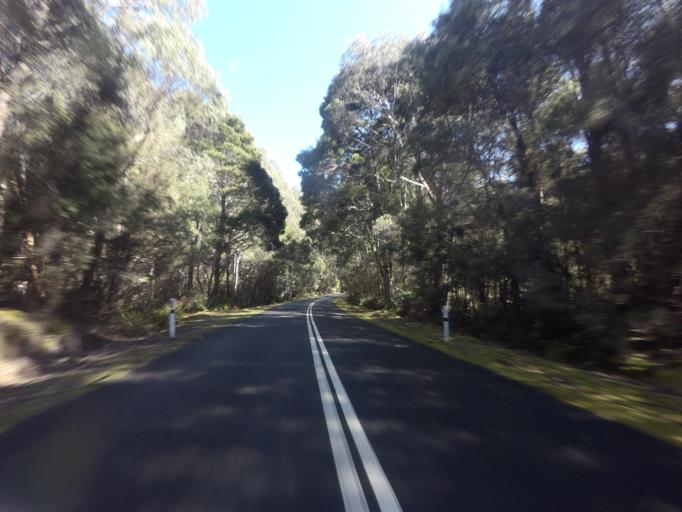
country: AU
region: Tasmania
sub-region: Derwent Valley
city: New Norfolk
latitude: -42.7538
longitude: 146.5243
